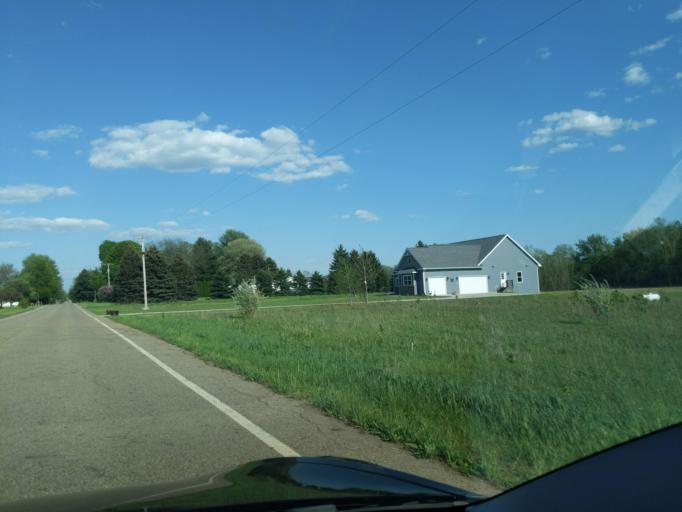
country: US
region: Michigan
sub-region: Eaton County
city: Dimondale
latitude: 42.6828
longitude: -84.6966
